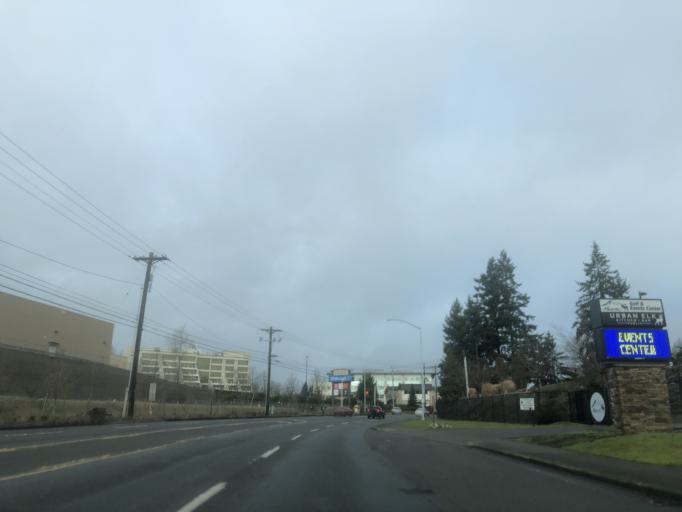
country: US
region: Washington
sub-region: Pierce County
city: Tacoma
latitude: 47.2394
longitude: -122.4769
